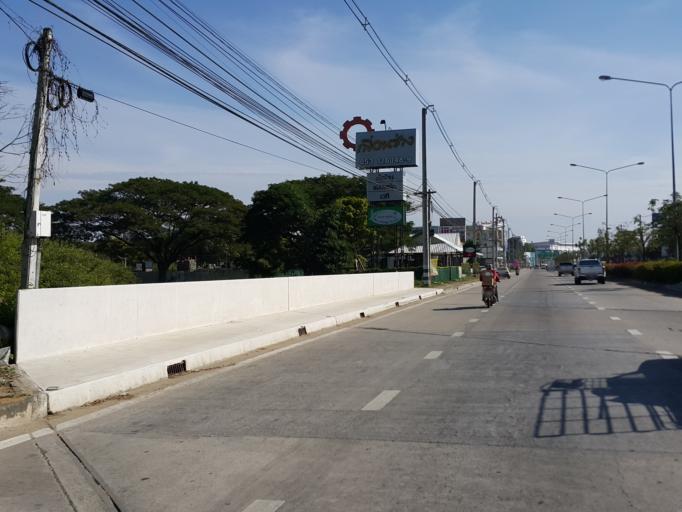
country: TH
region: Chiang Mai
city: Chiang Mai
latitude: 18.7892
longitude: 99.0398
